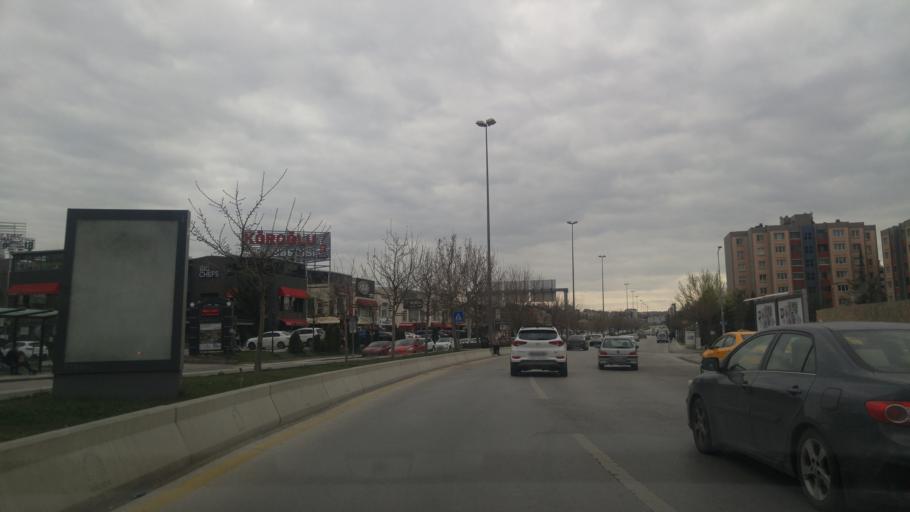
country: TR
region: Ankara
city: Etimesgut
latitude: 39.8731
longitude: 32.6880
